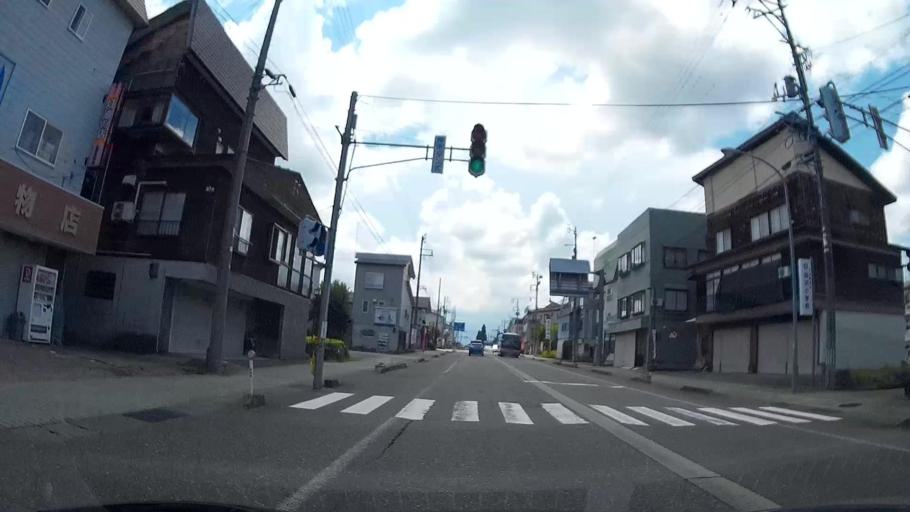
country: JP
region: Niigata
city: Tokamachi
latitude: 37.0526
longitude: 138.6971
